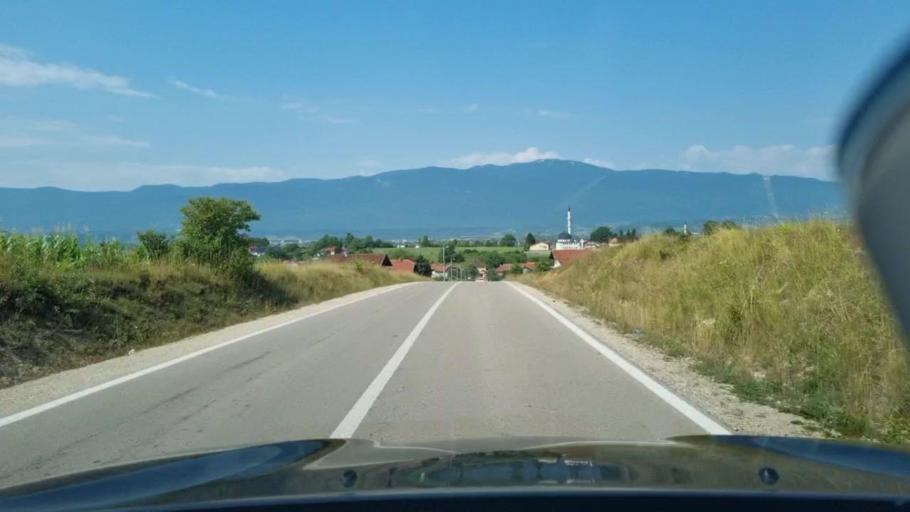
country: BA
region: Federation of Bosnia and Herzegovina
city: Bihac
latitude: 44.8422
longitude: 15.8975
